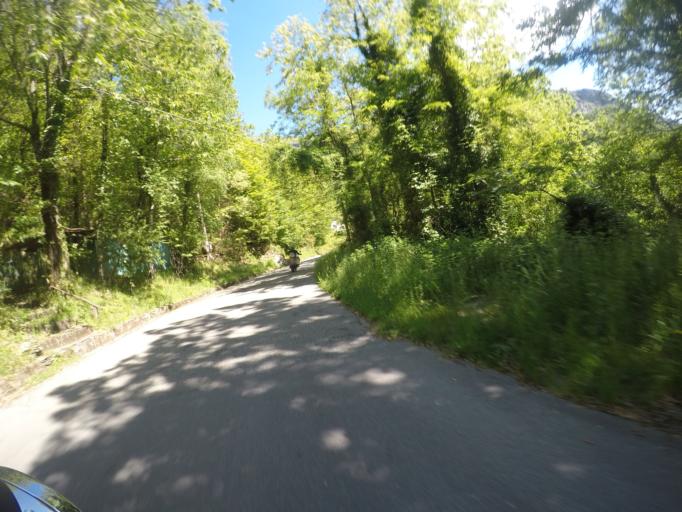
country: IT
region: Tuscany
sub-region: Provincia di Lucca
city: Fontana delle Monache
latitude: 44.0653
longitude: 10.3079
